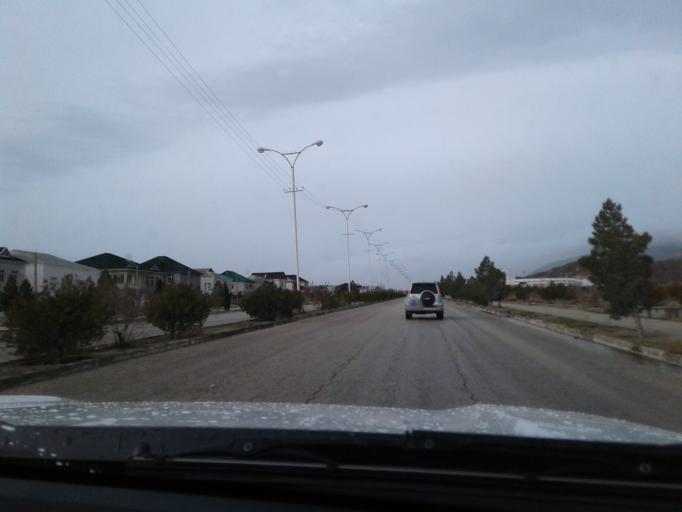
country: TM
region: Balkan
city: Balkanabat
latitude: 39.5342
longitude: 54.3530
